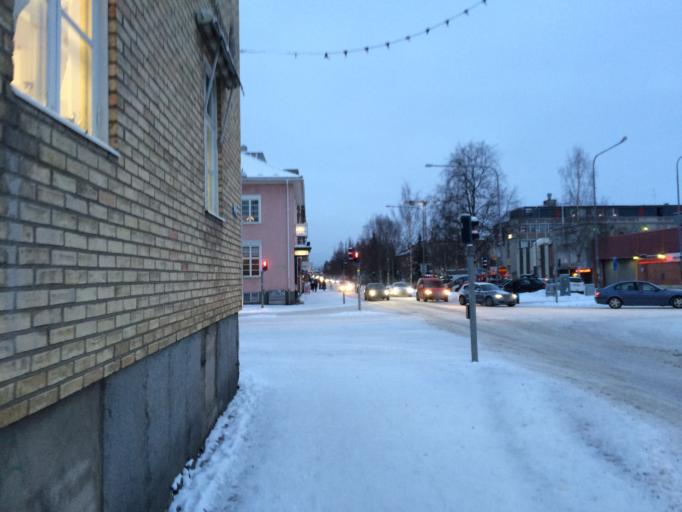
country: SE
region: Vaesterbotten
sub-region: Skelleftea Kommun
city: Skelleftea
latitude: 64.7521
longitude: 20.9506
